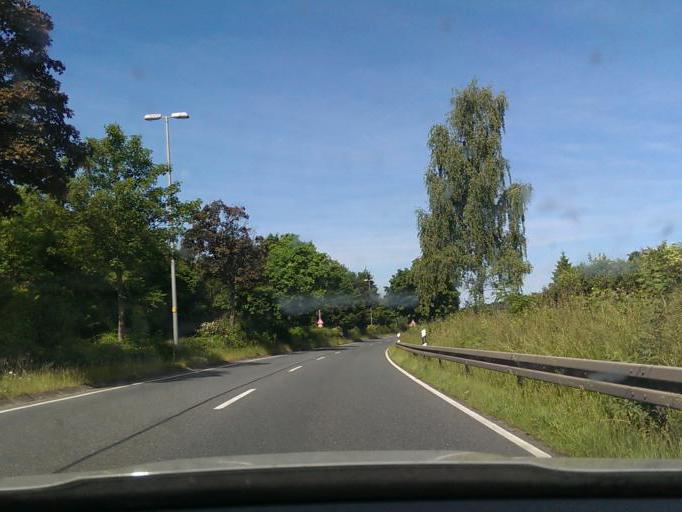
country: DE
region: Lower Saxony
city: Hildesheim
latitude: 52.1571
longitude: 9.9109
